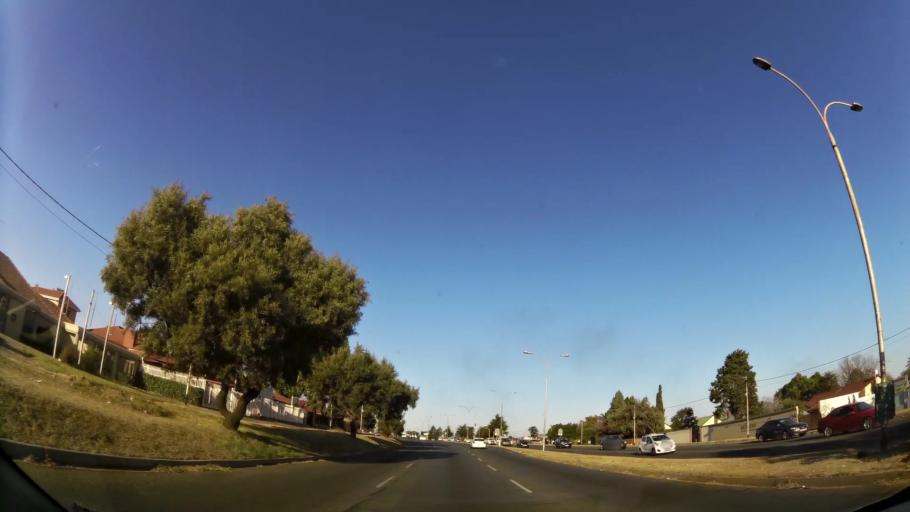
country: ZA
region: Gauteng
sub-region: City of Johannesburg Metropolitan Municipality
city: Roodepoort
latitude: -26.1448
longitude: 27.8795
